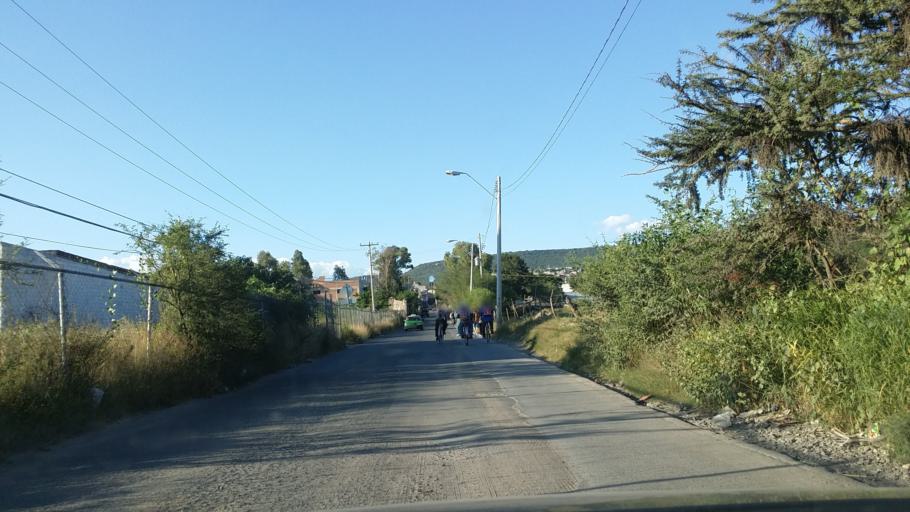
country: MX
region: Guanajuato
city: Leon
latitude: 21.1948
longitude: -101.6792
